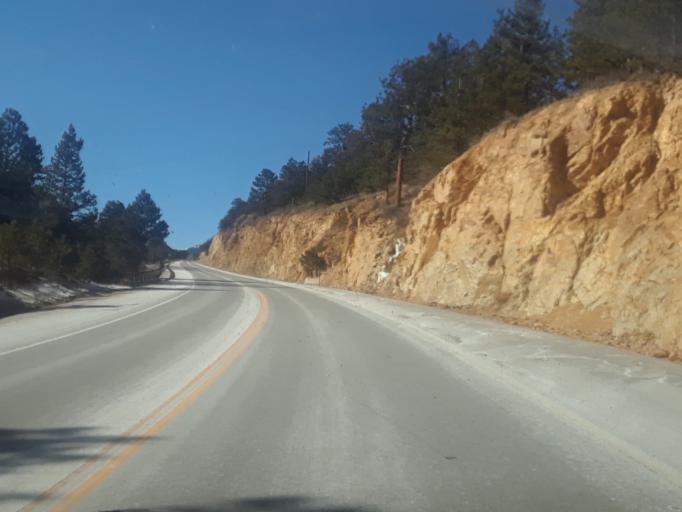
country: US
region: Colorado
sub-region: Larimer County
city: Estes Park
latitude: 40.1926
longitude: -105.5119
